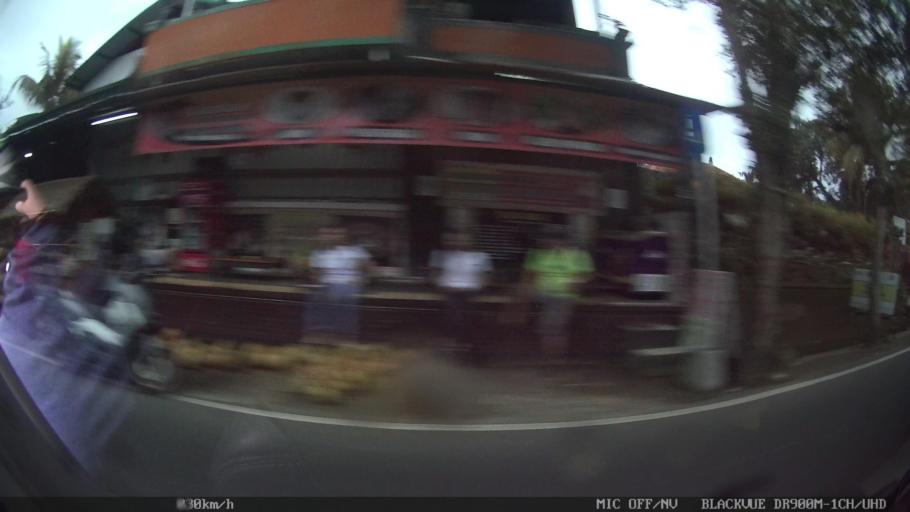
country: ID
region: Bali
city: Badung
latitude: -8.4223
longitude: 115.2451
